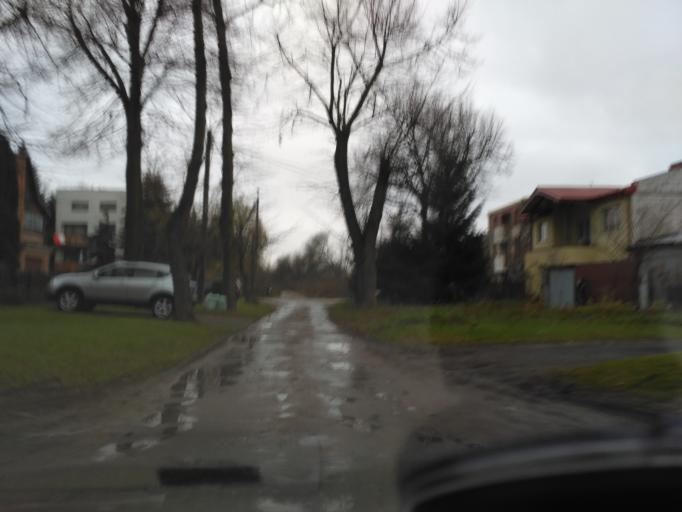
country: PL
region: Lublin Voivodeship
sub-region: Powiat lubelski
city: Lublin
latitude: 51.2656
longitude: 22.5406
